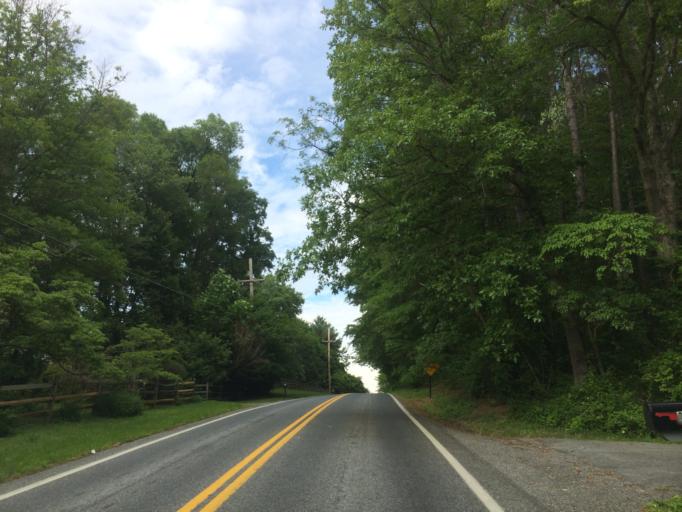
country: US
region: Maryland
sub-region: Howard County
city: Riverside
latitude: 39.1799
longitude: -76.9053
